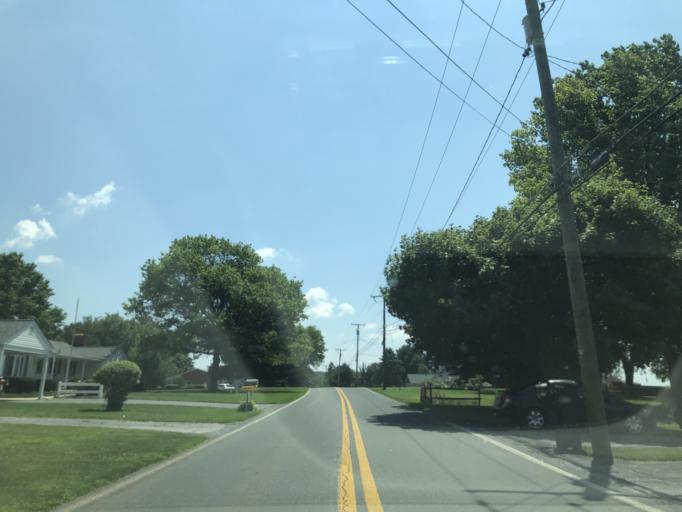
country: US
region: Maryland
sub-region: Carroll County
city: Westminster
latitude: 39.5396
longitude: -76.9796
